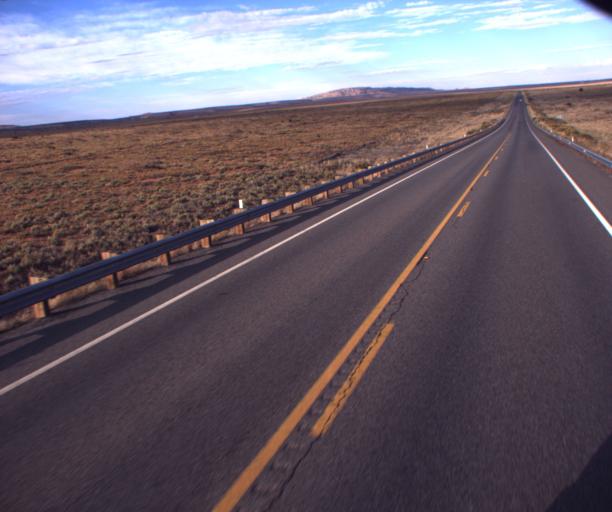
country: US
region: Arizona
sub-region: Apache County
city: Lukachukai
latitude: 36.9281
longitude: -109.1964
